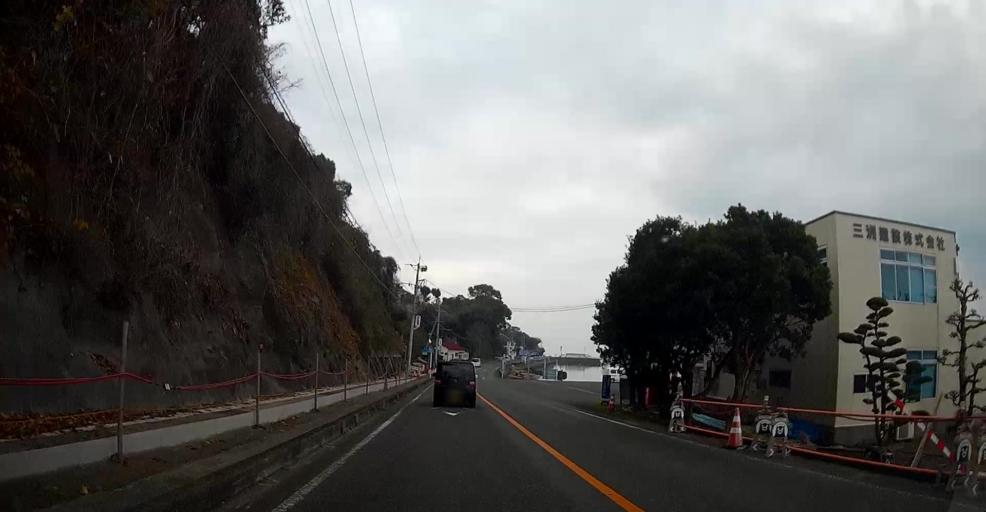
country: JP
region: Kumamoto
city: Yatsushiro
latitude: 32.6125
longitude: 130.4945
